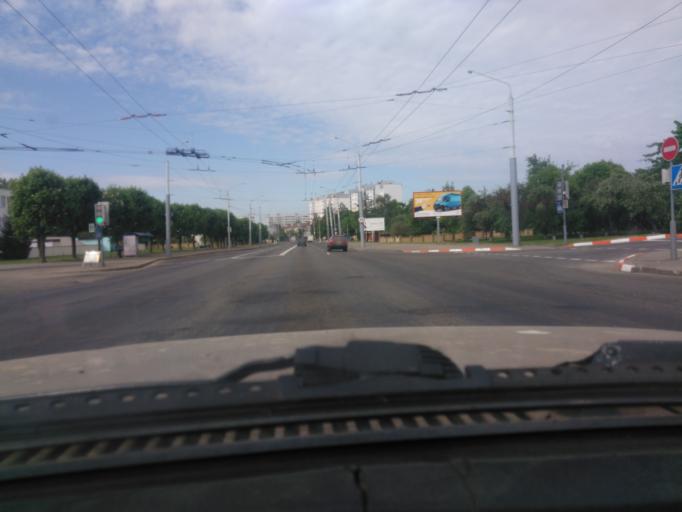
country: BY
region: Mogilev
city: Buynichy
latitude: 53.8883
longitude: 30.2818
